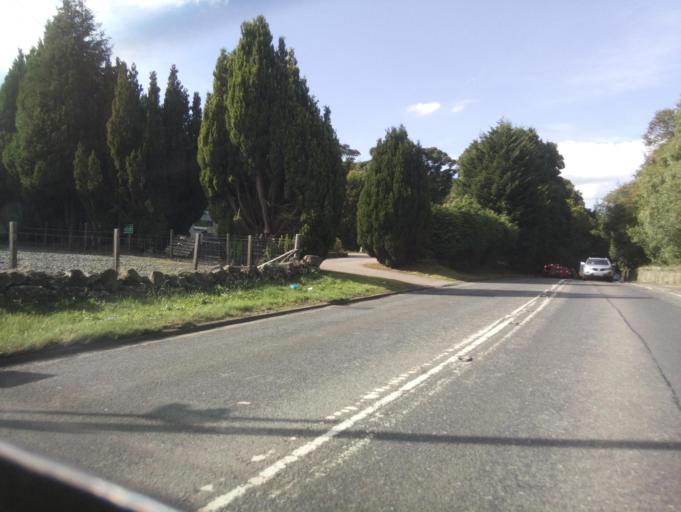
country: GB
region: Scotland
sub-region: Stirling
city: Cowie
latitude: 56.0376
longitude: -3.8572
